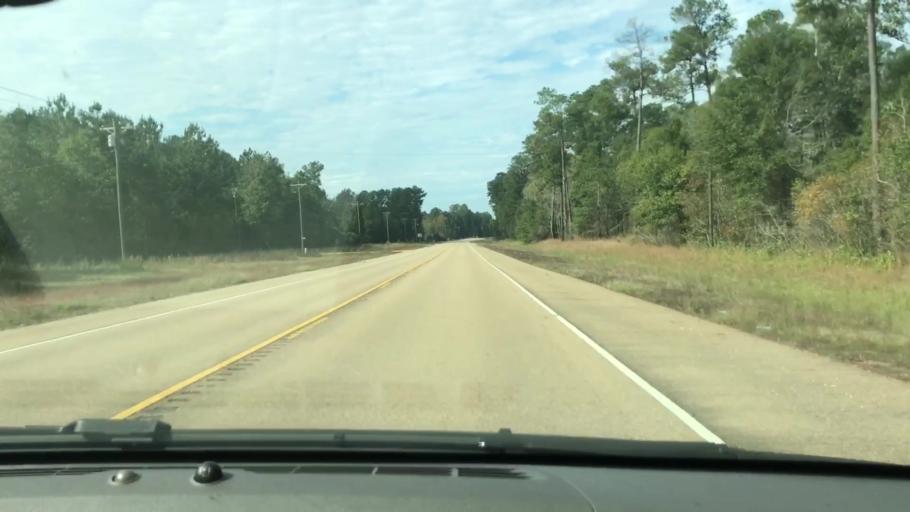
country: US
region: Louisiana
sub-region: Saint Tammany Parish
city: Abita Springs
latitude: 30.5058
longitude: -89.9693
